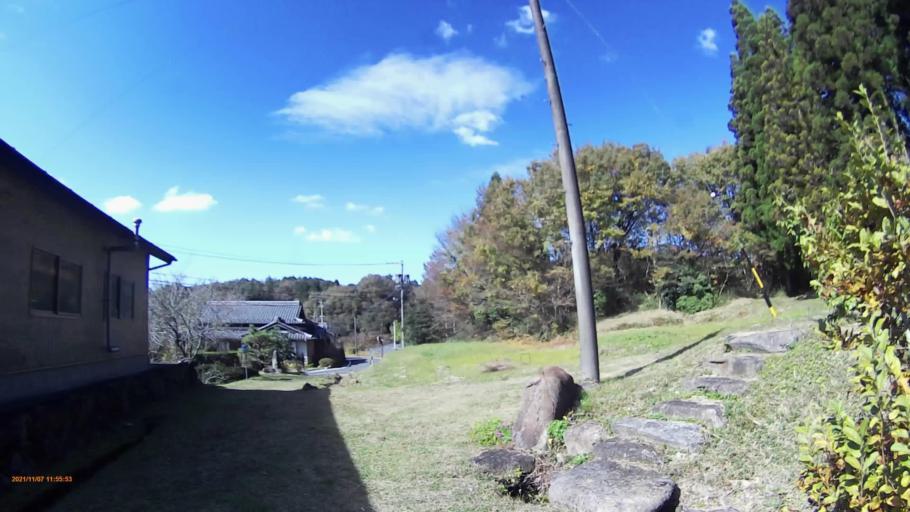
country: JP
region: Gifu
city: Mizunami
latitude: 35.4365
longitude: 137.2771
